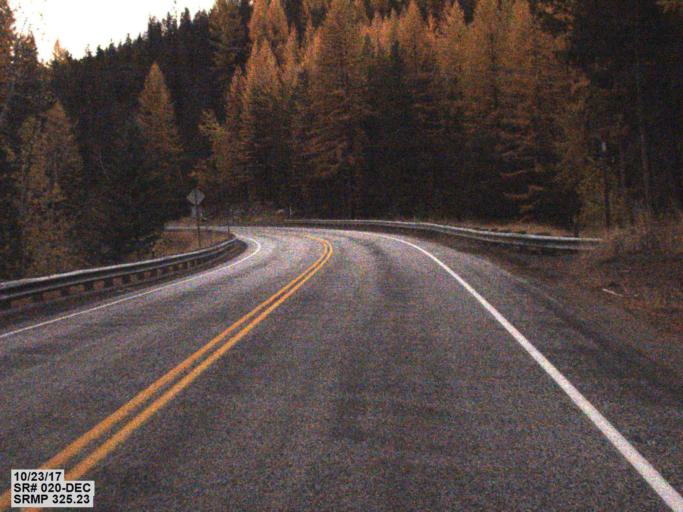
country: US
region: Washington
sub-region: Ferry County
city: Republic
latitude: 48.6243
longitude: -118.4182
